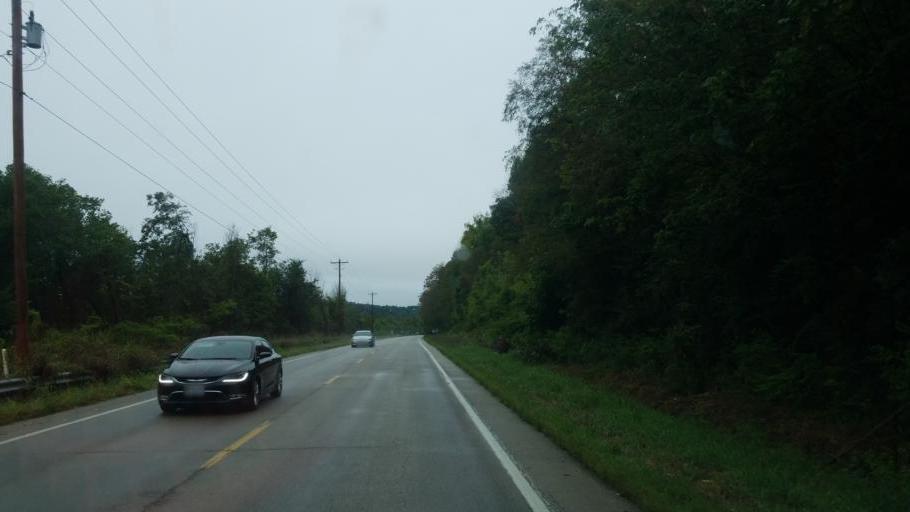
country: US
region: Kentucky
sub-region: Mason County
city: Maysville
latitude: 38.6505
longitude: -83.7463
